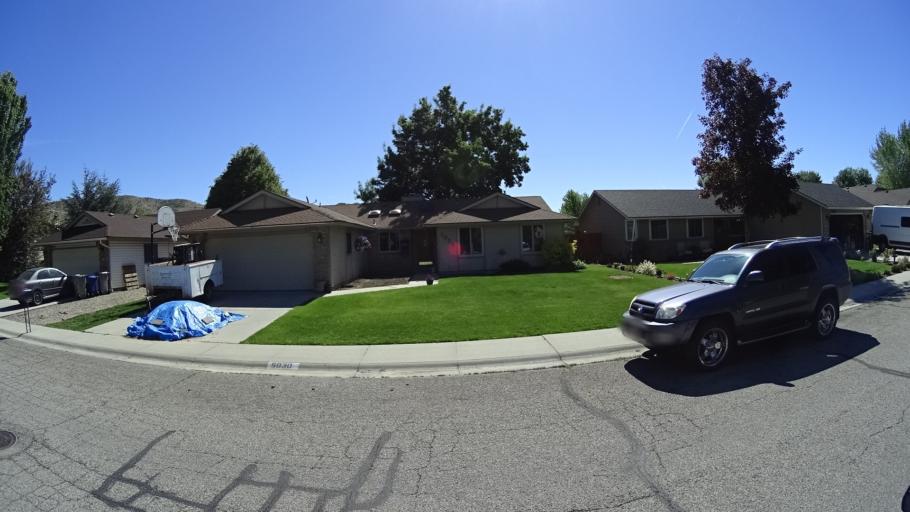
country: US
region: Idaho
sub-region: Ada County
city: Garden City
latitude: 43.6659
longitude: -116.2615
